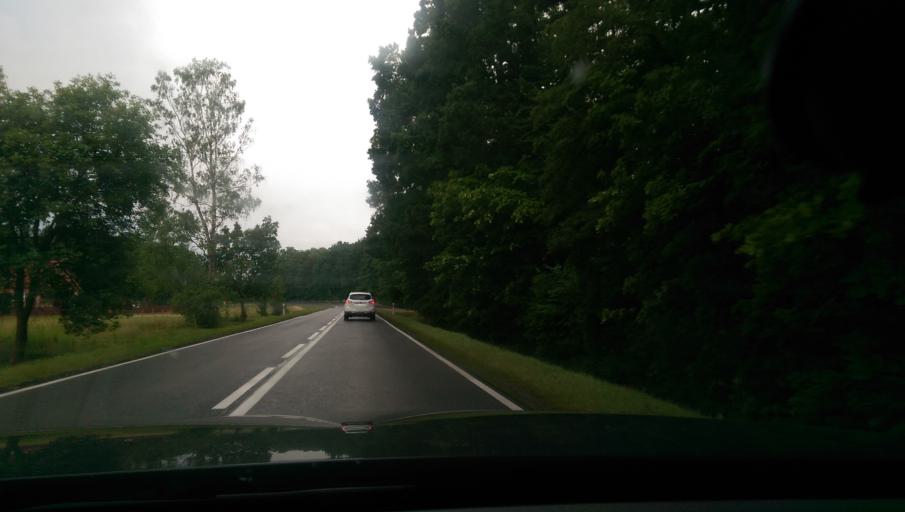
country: PL
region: Warmian-Masurian Voivodeship
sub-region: Powiat szczycienski
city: Szczytno
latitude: 53.5388
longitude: 20.9862
